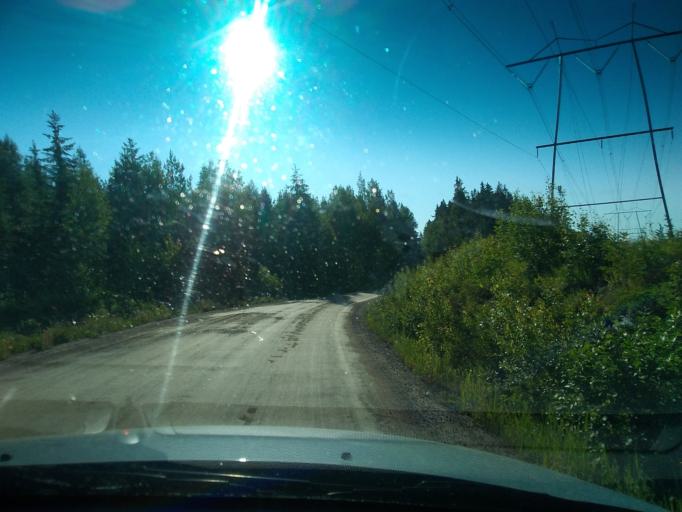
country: FI
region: Haeme
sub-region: Forssa
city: Tammela
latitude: 60.7565
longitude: 23.7540
